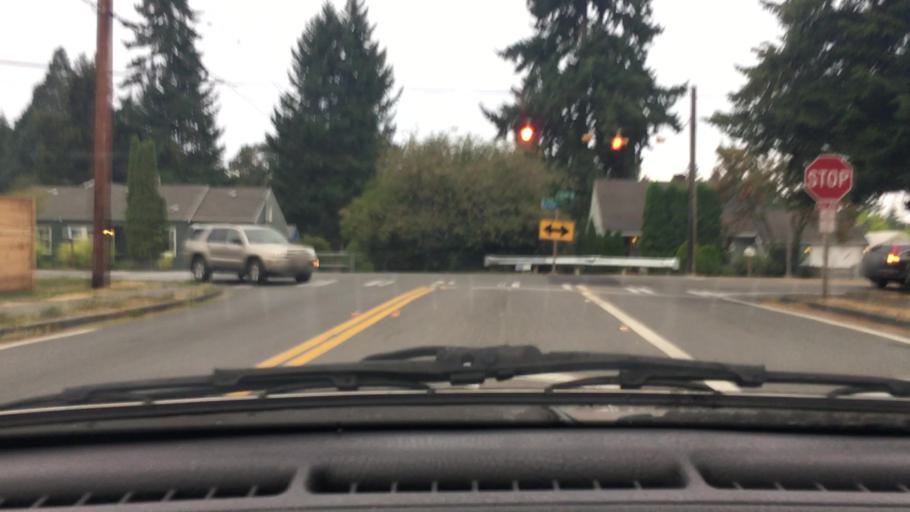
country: US
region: Washington
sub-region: King County
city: Burien
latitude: 47.4595
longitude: -122.3575
